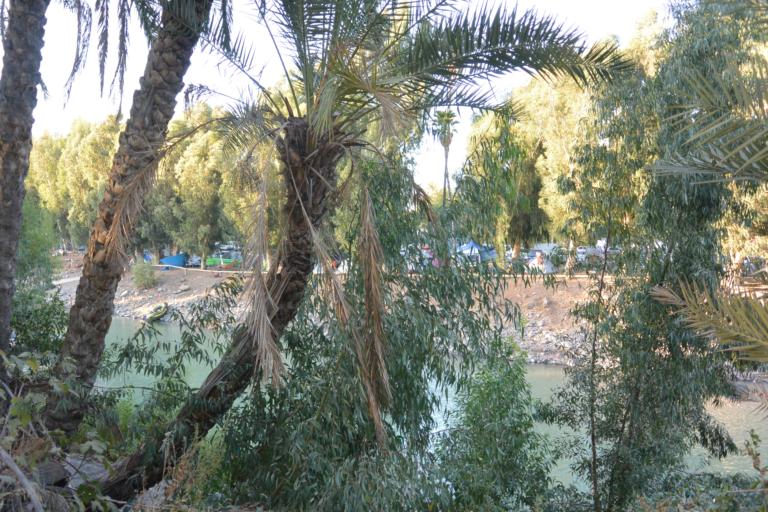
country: IL
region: Northern District
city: Yavne'el
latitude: 32.7101
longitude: 35.5767
